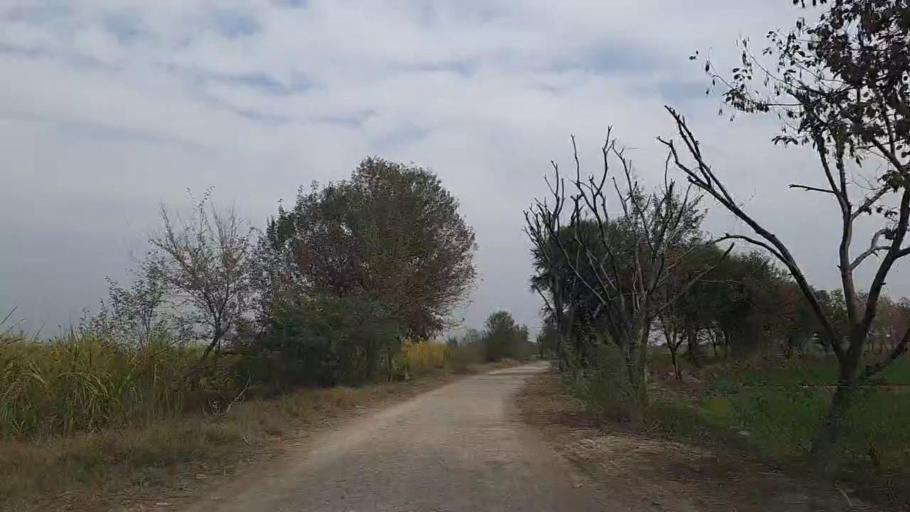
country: PK
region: Sindh
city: Daur
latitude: 26.4241
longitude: 68.4574
